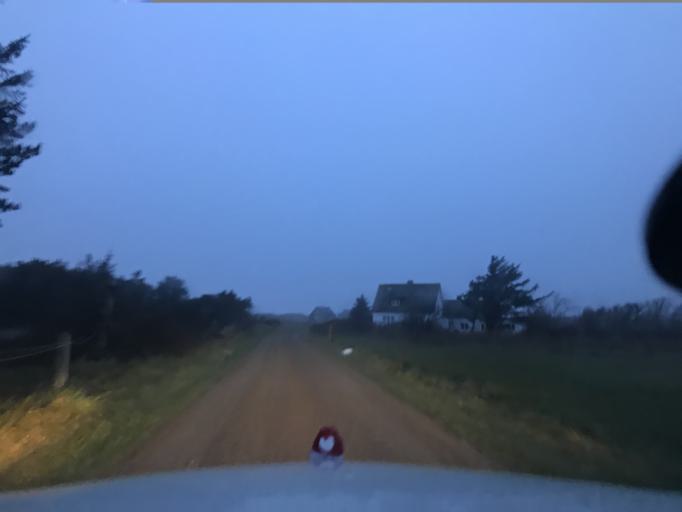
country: DK
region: South Denmark
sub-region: Esbjerg Kommune
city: Tjaereborg
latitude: 55.2700
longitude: 8.5390
